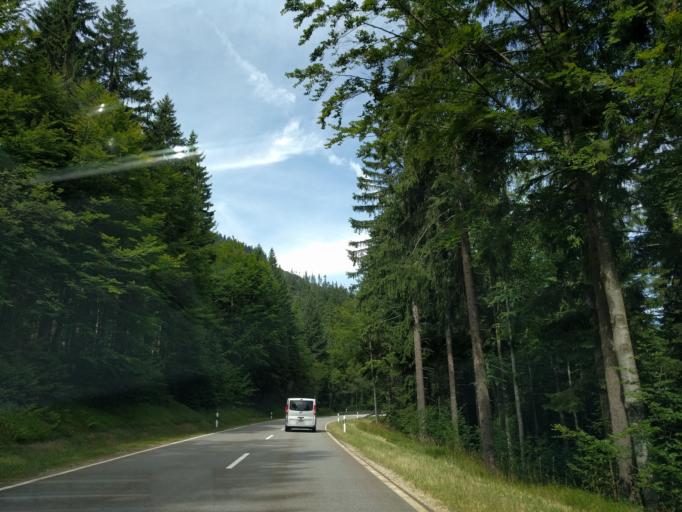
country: DE
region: Bavaria
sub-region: Lower Bavaria
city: Bayerisch Eisenstein
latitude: 49.1147
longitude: 13.1529
